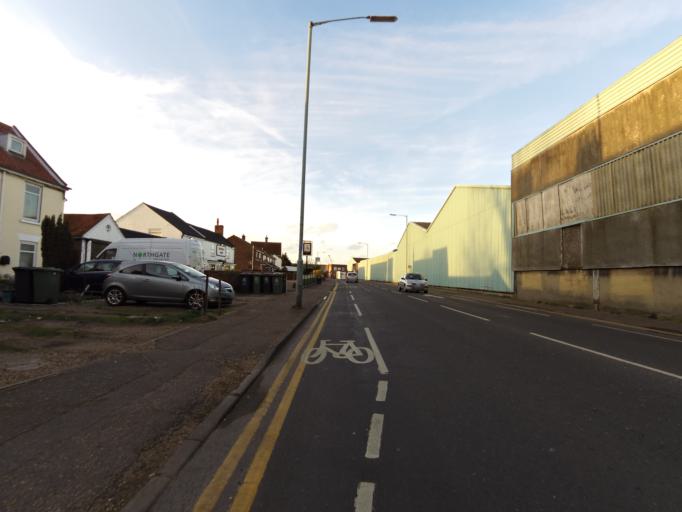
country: GB
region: England
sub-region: Norfolk
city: Great Yarmouth
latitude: 52.5956
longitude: 1.7252
